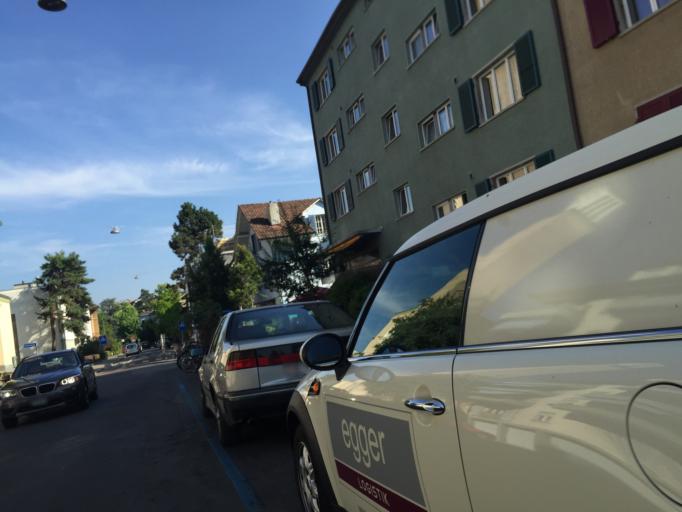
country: CH
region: Bern
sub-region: Bern-Mittelland District
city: Bern
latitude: 46.9599
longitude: 7.4489
